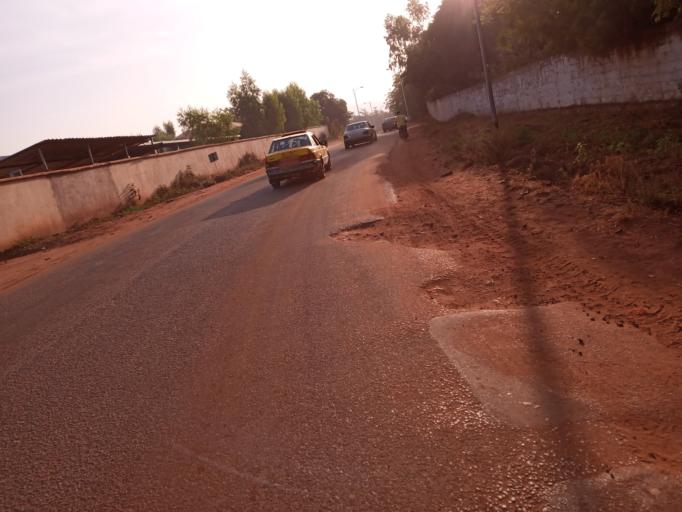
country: ML
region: Bamako
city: Bamako
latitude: 12.6363
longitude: -7.9261
